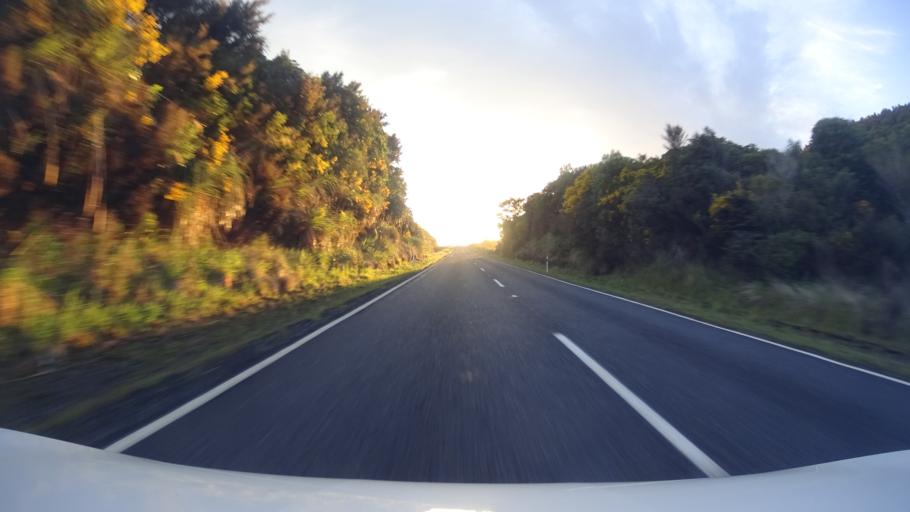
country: NZ
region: Waikato
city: Turangi
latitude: -39.0631
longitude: 175.6433
